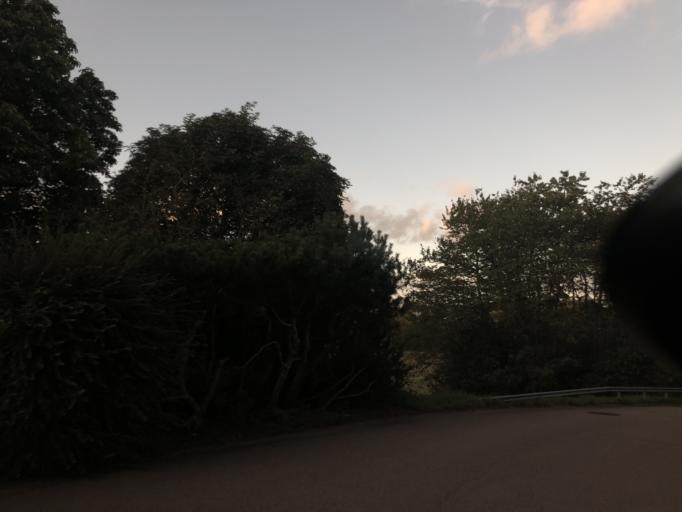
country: SE
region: Vaestra Goetaland
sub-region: Goteborg
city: Goeteborg
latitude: 57.7611
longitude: 11.9311
